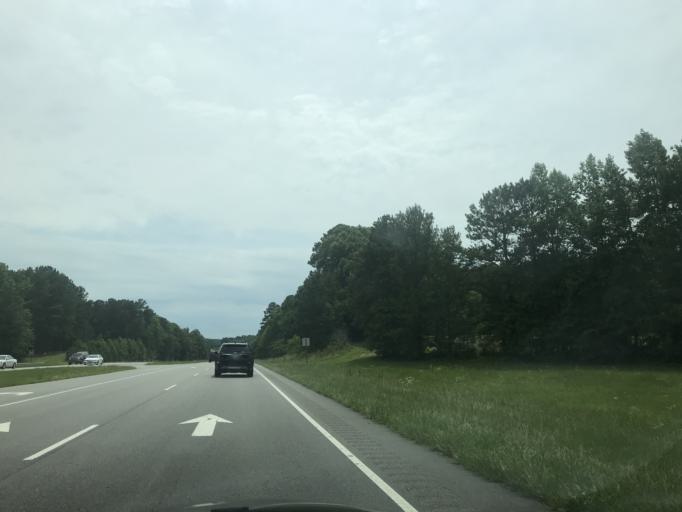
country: US
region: North Carolina
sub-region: Vance County
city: South Henderson
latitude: 36.2585
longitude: -78.4246
